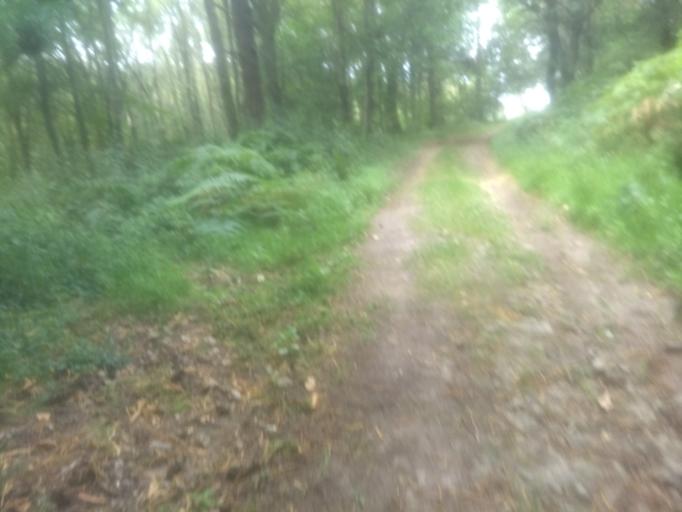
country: FR
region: Limousin
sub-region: Departement de la Haute-Vienne
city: Ambazac
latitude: 46.0347
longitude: 1.5197
